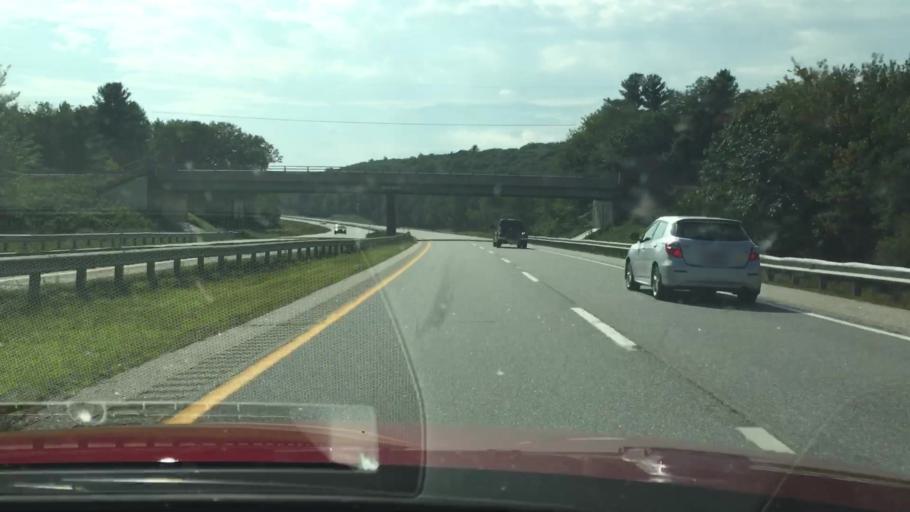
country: US
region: Maine
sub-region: Androscoggin County
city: Sabattus
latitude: 44.1243
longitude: -70.0347
